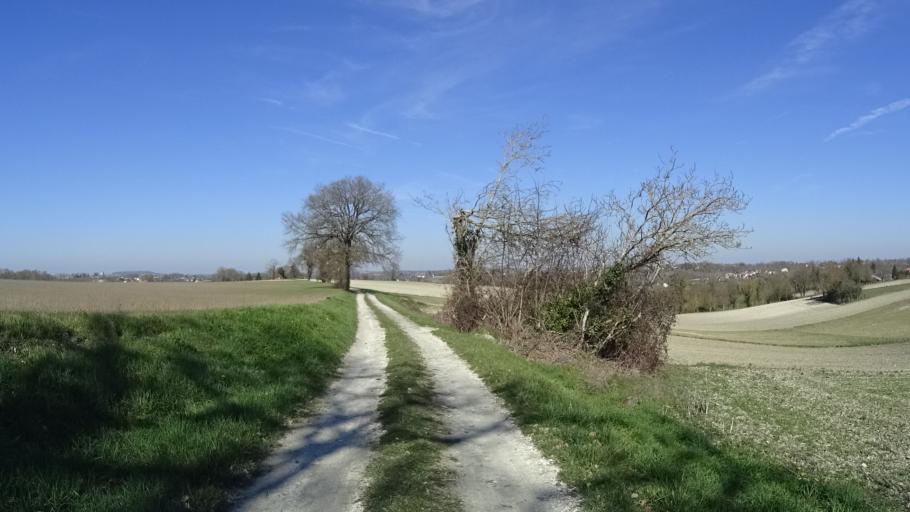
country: FR
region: Aquitaine
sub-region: Departement de la Dordogne
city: Riberac
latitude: 45.2275
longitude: 0.3451
